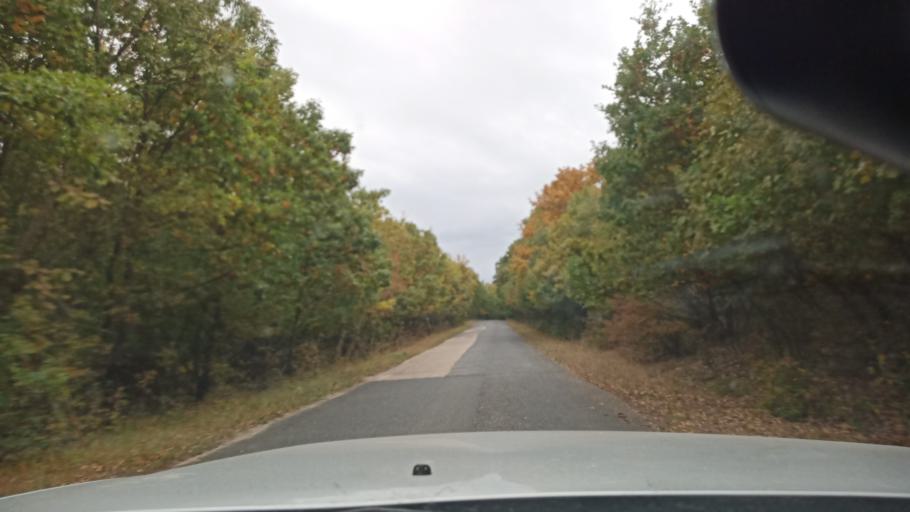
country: HU
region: Fejer
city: Zamoly
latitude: 47.3567
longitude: 18.3489
